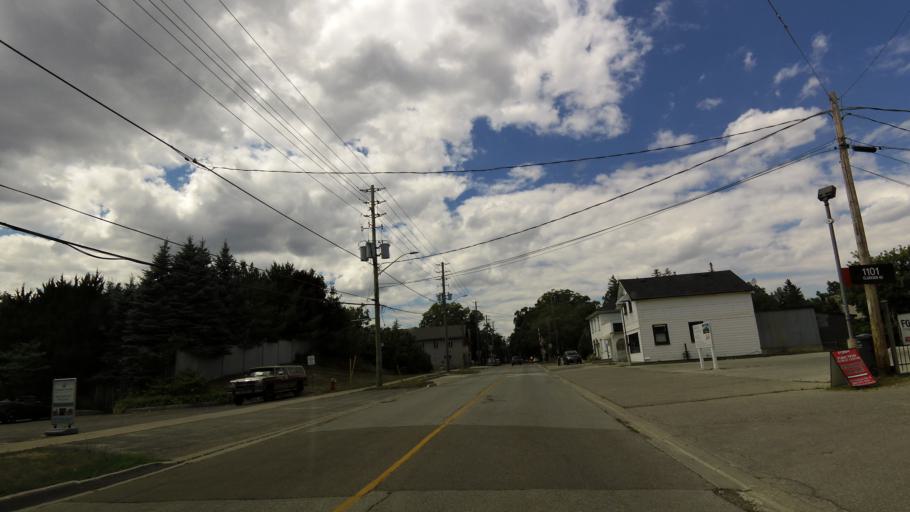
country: CA
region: Ontario
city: Mississauga
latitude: 43.5190
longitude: -79.6258
